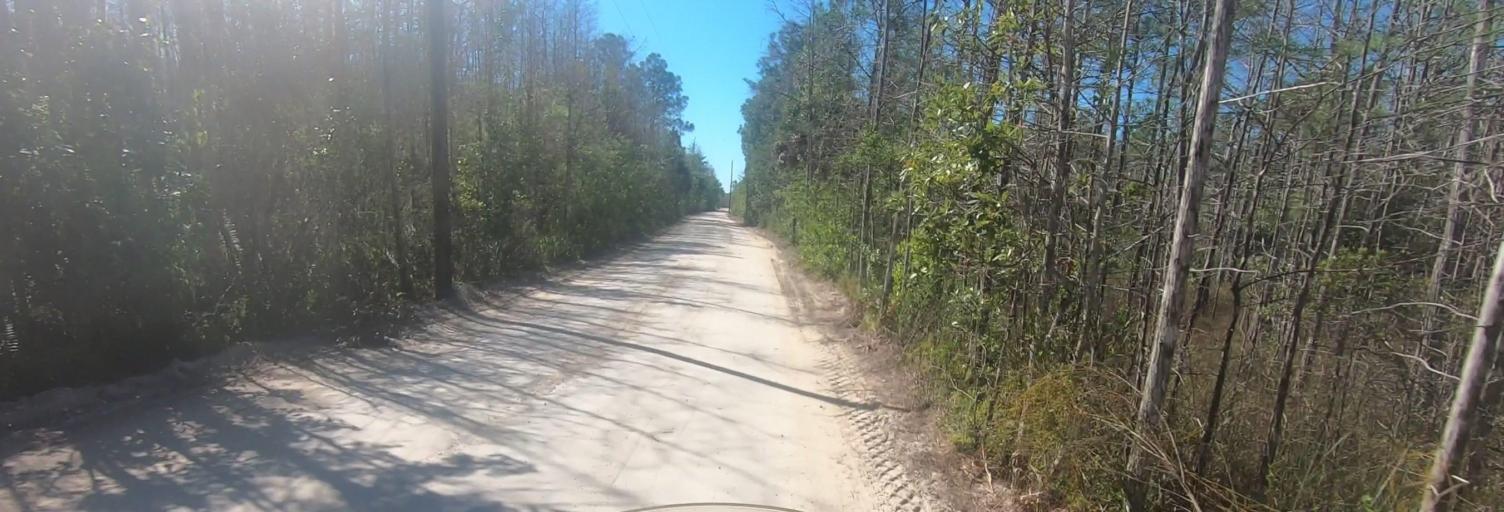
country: US
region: Florida
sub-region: Collier County
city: Lely Resort
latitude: 25.8901
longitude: -81.2299
